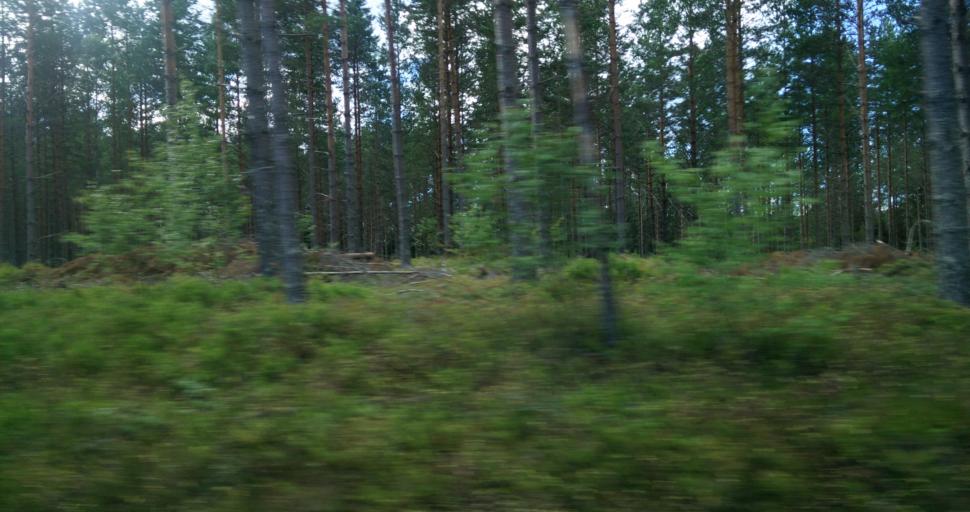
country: SE
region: Vaermland
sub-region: Hagfors Kommun
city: Hagfors
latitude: 60.0310
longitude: 13.5418
